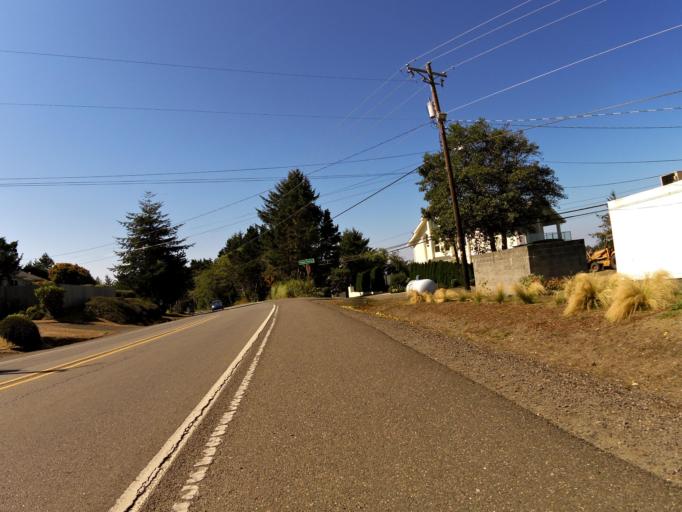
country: US
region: Oregon
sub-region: Coos County
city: Barview
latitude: 43.3595
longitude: -124.3062
